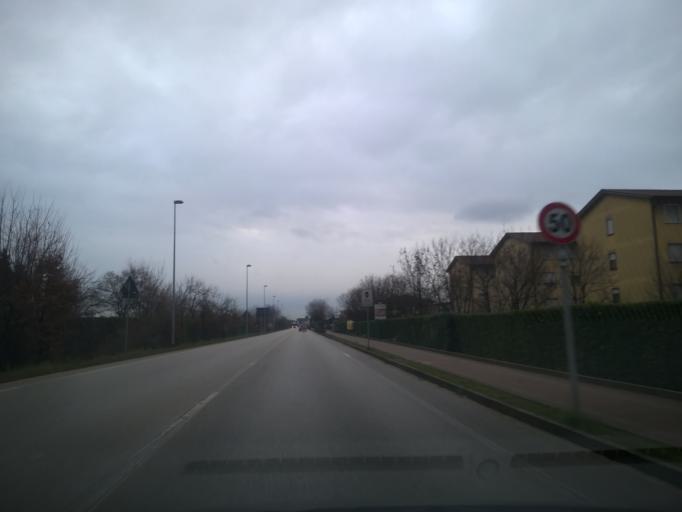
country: IT
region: Veneto
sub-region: Provincia di Vicenza
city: Marano Vicentino
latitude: 45.6974
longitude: 11.4425
